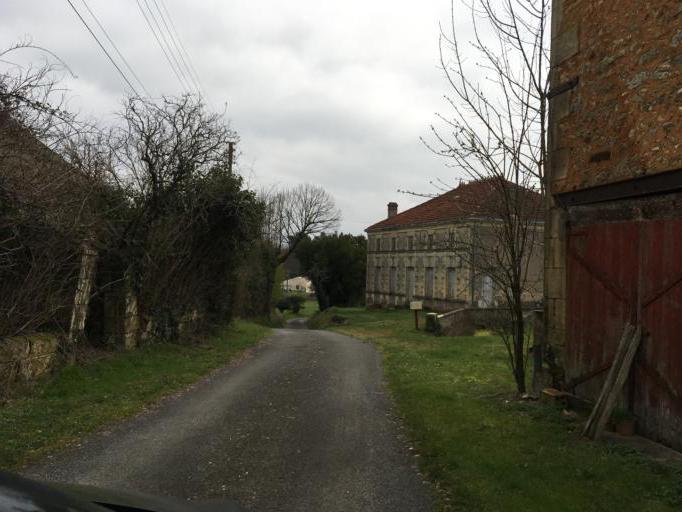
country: FR
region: Poitou-Charentes
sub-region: Departement de la Charente-Maritime
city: Mirambeau
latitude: 45.3358
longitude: -0.5807
